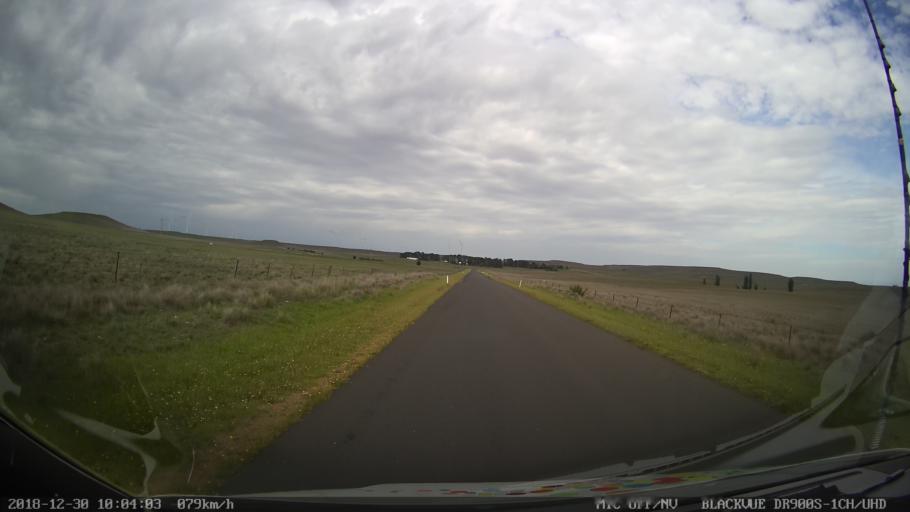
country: AU
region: New South Wales
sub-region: Cooma-Monaro
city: Cooma
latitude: -36.5186
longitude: 149.1502
